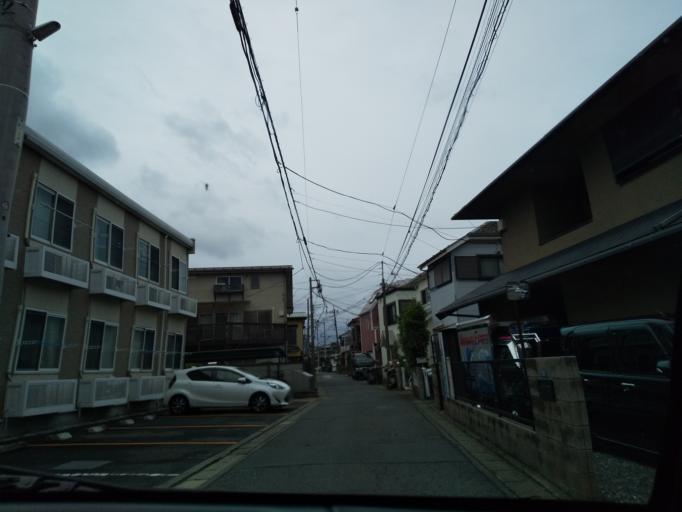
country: JP
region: Kanagawa
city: Minami-rinkan
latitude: 35.4319
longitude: 139.4434
